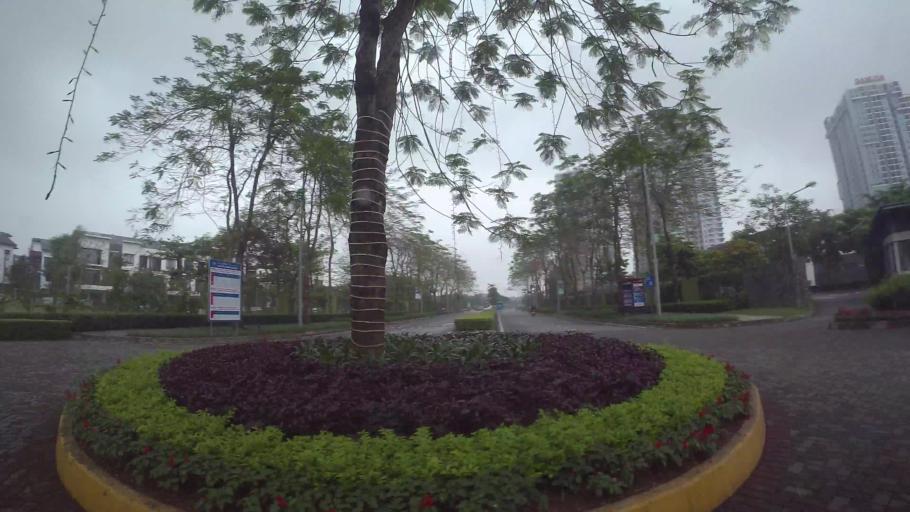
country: VN
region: Ha Noi
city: Van Dien
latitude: 20.9729
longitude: 105.8765
